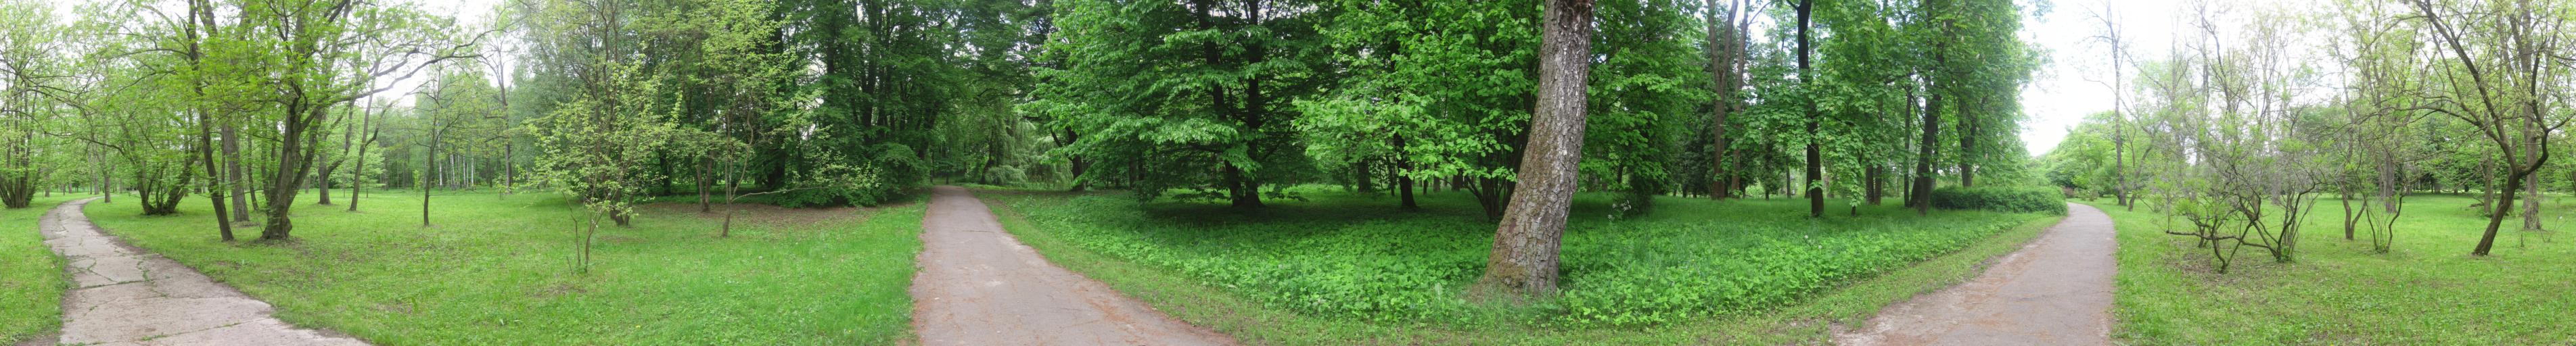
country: LT
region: Kauno apskritis
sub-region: Kaunas
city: Aleksotas
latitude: 54.8703
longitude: 23.9052
